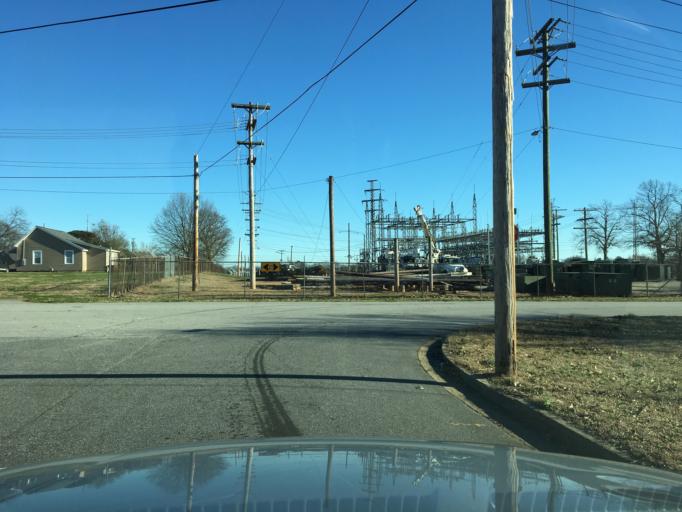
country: US
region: South Carolina
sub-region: Greenville County
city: Greer
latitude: 34.9383
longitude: -82.2354
